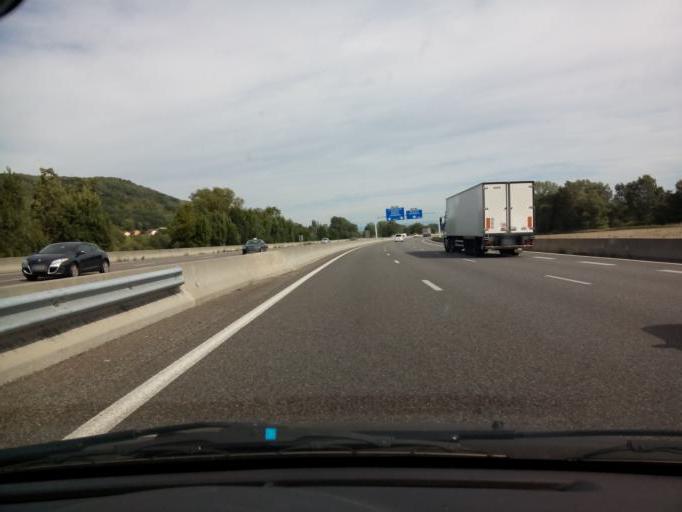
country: FR
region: Rhone-Alpes
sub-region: Departement de l'Isere
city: Ruy
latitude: 45.5715
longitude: 5.3302
